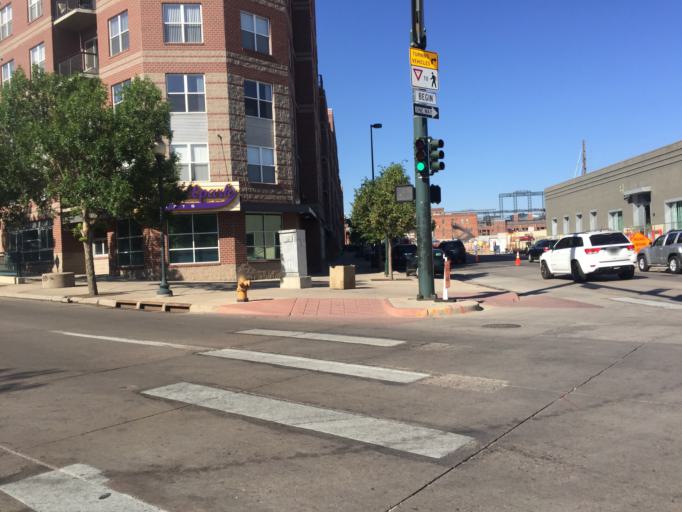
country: US
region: Colorado
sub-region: Denver County
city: Denver
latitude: 39.7593
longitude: -104.9877
